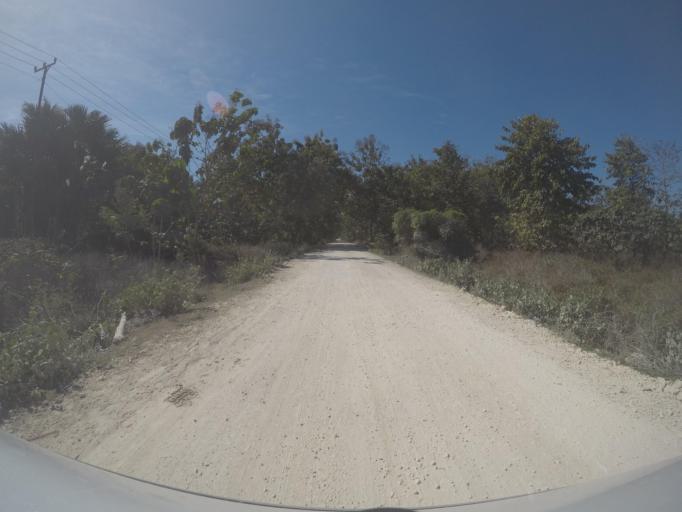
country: TL
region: Viqueque
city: Viqueque
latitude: -8.8867
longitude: 126.5071
